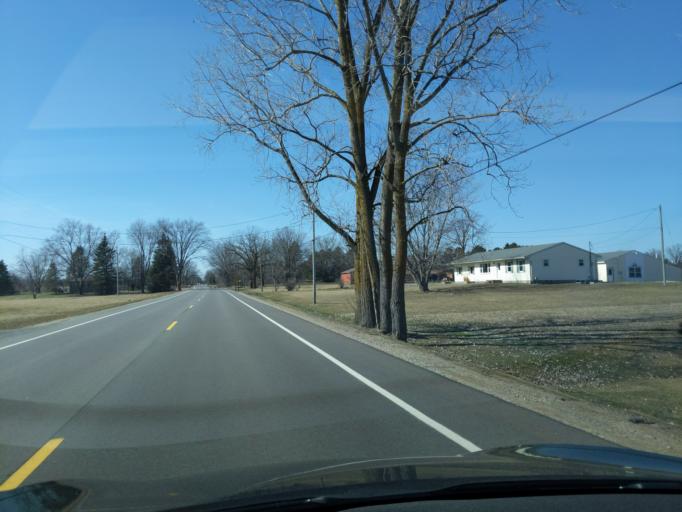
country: US
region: Michigan
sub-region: Eaton County
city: Grand Ledge
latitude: 42.7264
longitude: -84.7163
